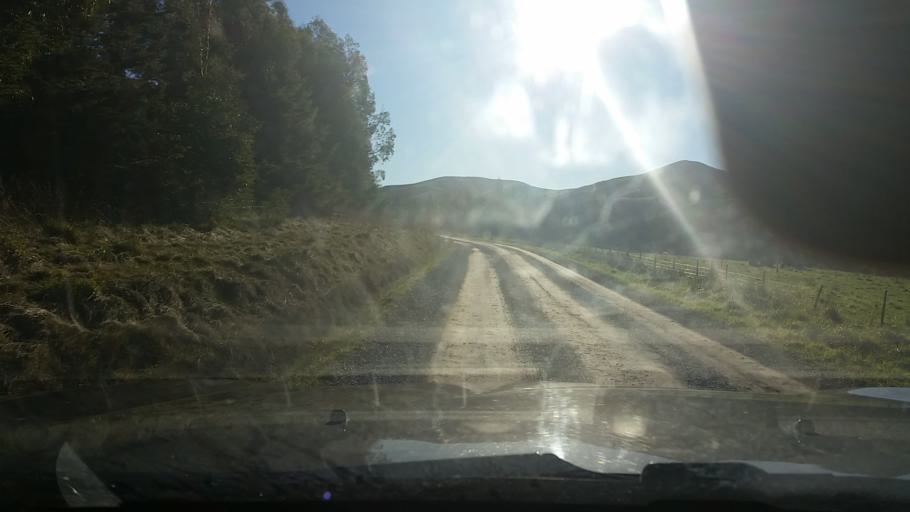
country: NZ
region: Marlborough
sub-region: Marlborough District
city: Blenheim
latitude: -41.5910
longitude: 174.0957
